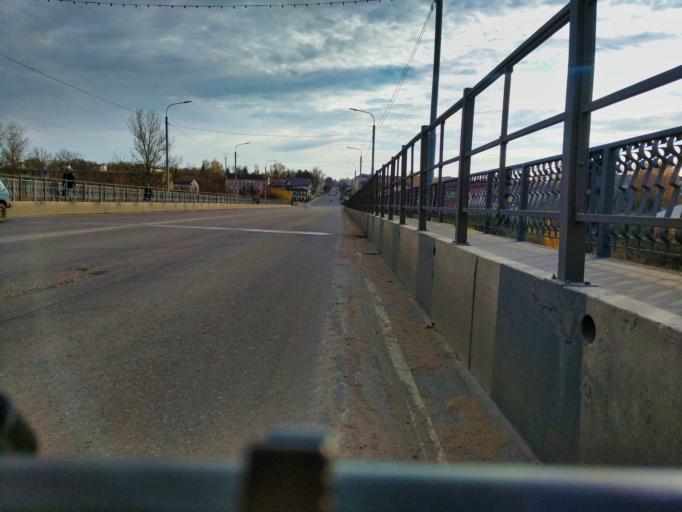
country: RU
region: Tverskaya
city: Rzhev
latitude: 56.2607
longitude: 34.3287
